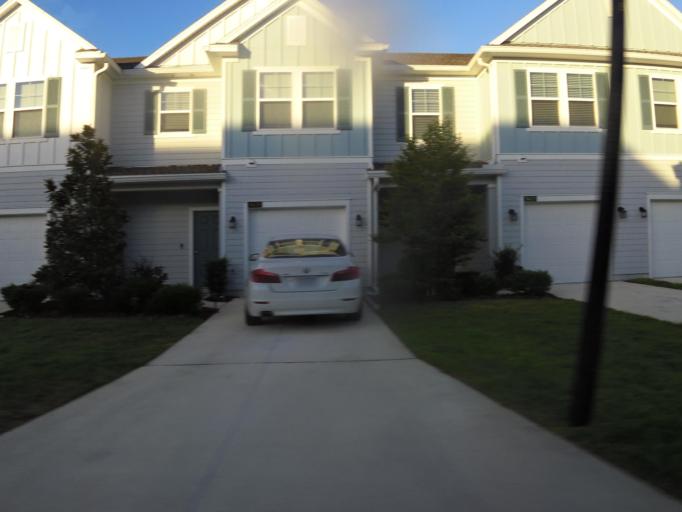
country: US
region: Florida
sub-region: Duval County
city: Jacksonville
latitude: 30.3095
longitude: -81.6109
